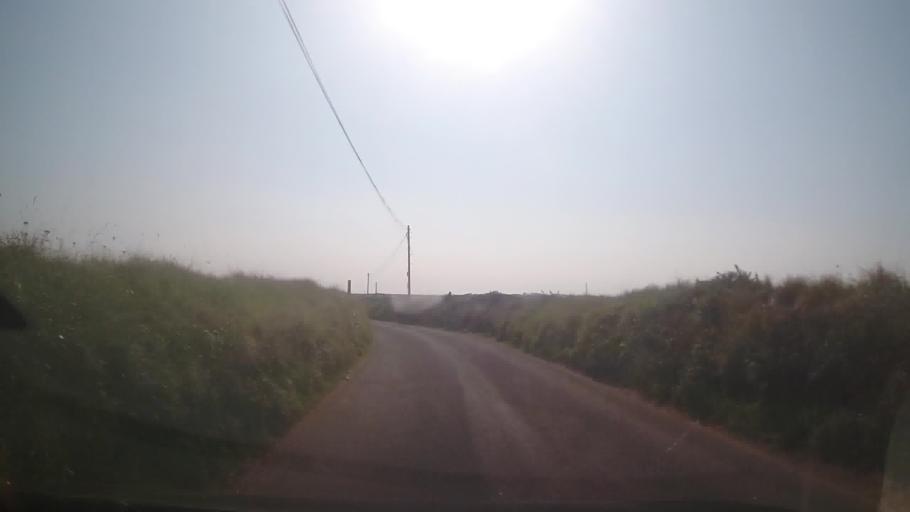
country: GB
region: Wales
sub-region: Pembrokeshire
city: Saint David's
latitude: 51.9033
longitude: -5.2451
